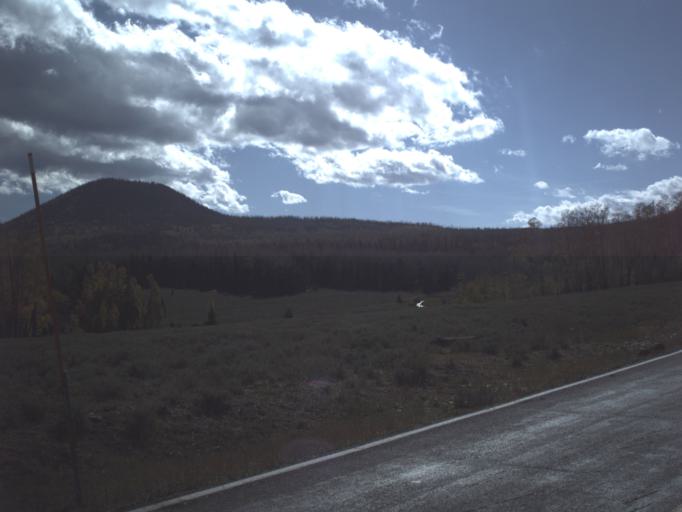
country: US
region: Utah
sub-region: Iron County
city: Parowan
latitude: 37.6588
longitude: -112.7449
